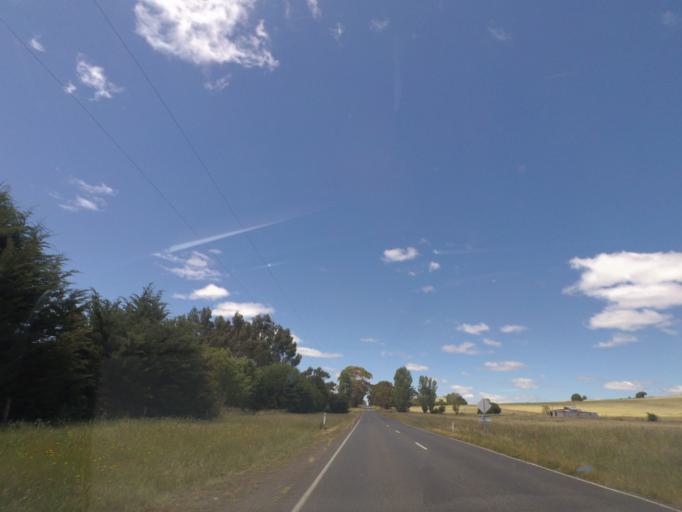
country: AU
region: Victoria
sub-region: Mount Alexander
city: Castlemaine
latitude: -37.3229
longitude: 144.1963
